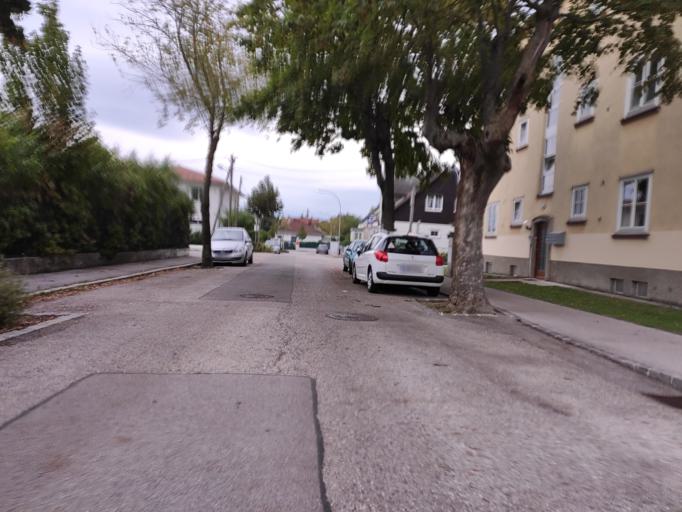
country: AT
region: Lower Austria
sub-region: Politischer Bezirk Baden
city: Baden
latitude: 48.0015
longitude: 16.2276
